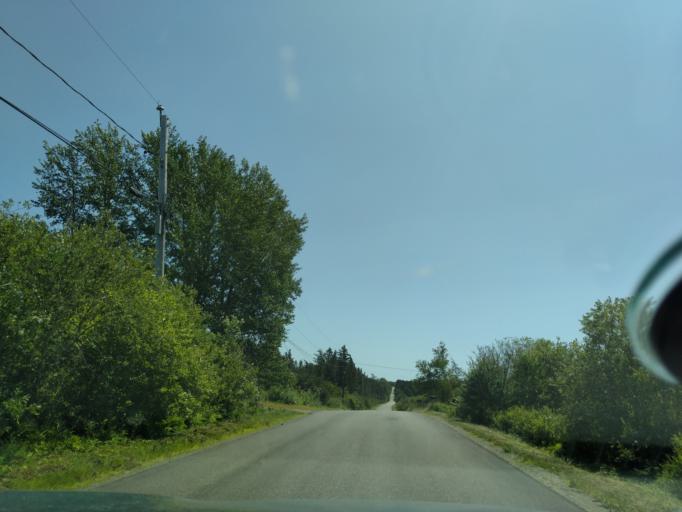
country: US
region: Maine
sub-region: Washington County
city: Eastport
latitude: 44.8395
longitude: -67.0139
